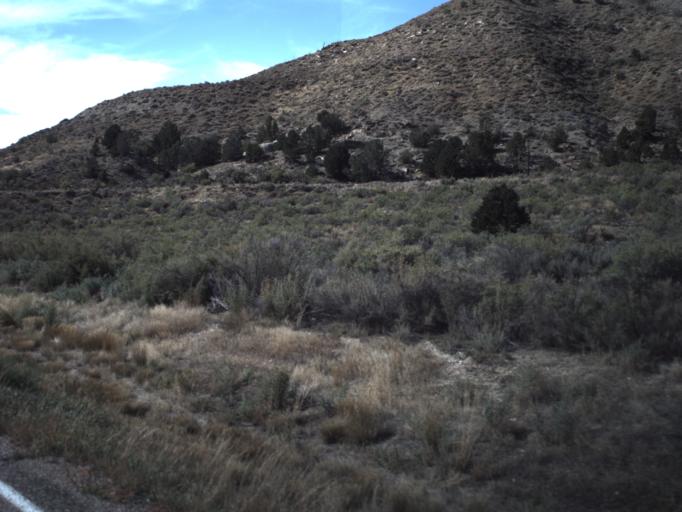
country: US
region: Utah
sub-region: Garfield County
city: Panguitch
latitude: 37.6044
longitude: -112.0606
